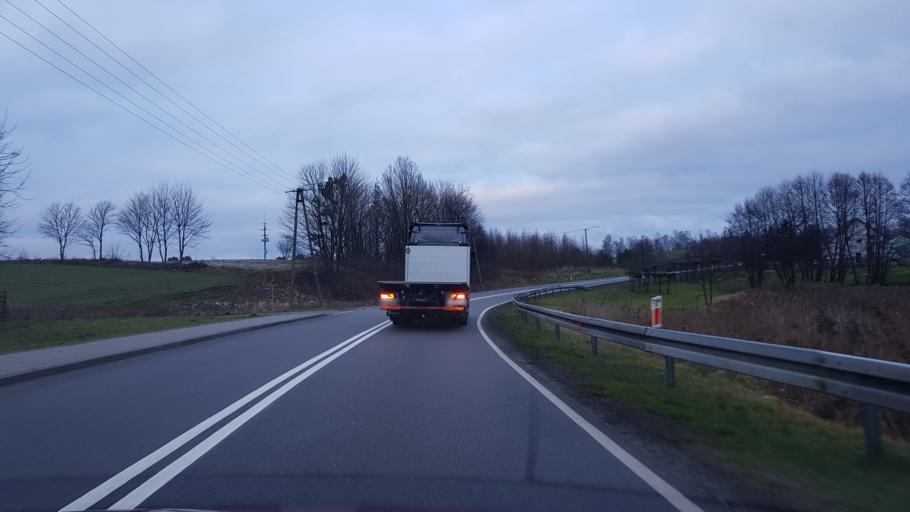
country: PL
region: Pomeranian Voivodeship
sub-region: Powiat bytowski
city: Tuchomie
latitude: 54.0460
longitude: 17.2041
